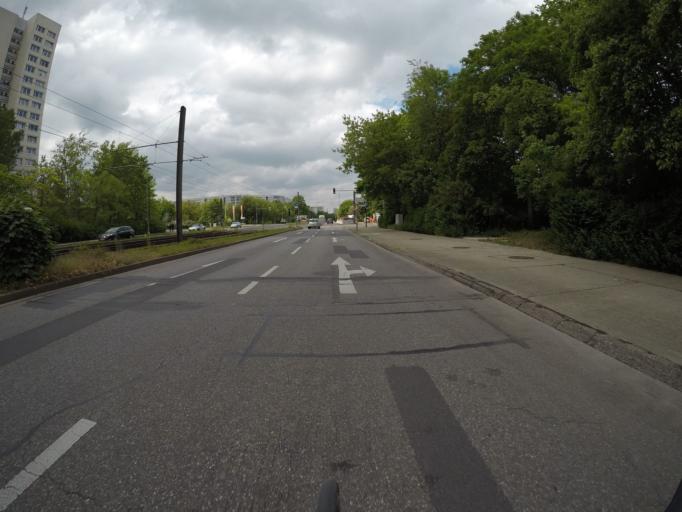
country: DE
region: Berlin
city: Marzahn
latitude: 52.5477
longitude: 13.5597
